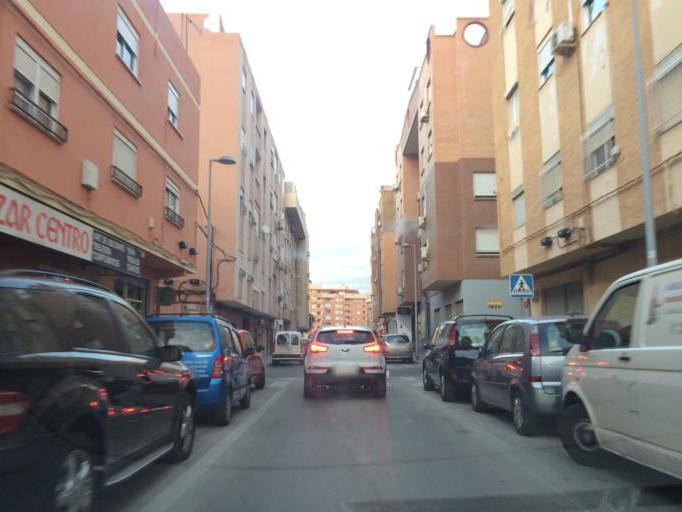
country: ES
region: Andalusia
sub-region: Provincia de Almeria
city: Almeria
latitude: 36.8343
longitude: -2.4523
